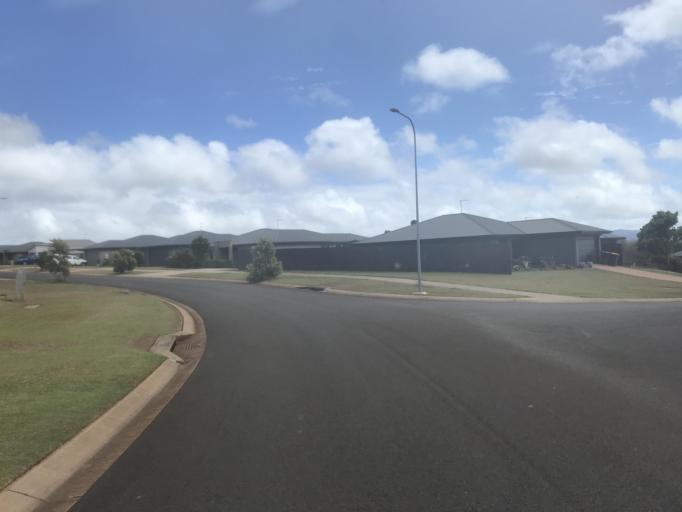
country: AU
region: Queensland
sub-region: Tablelands
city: Tolga
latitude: -17.2196
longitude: 145.4751
